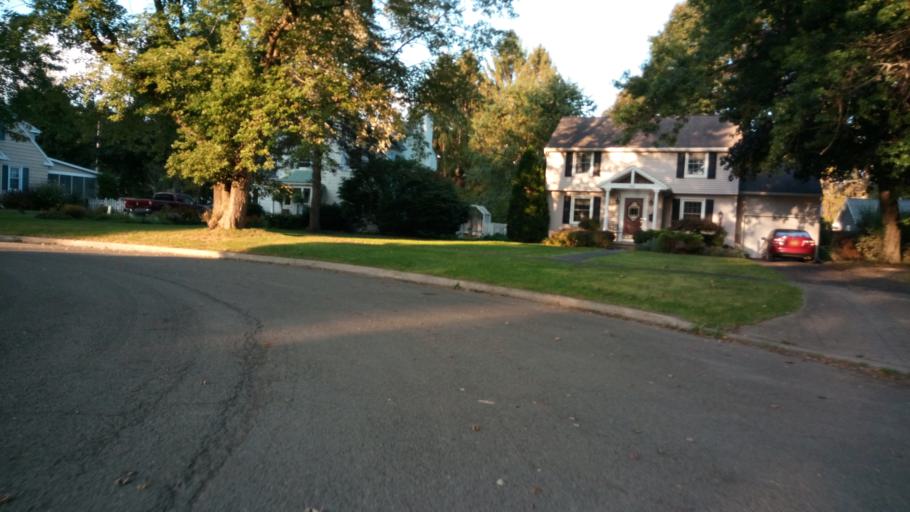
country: US
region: New York
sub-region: Chemung County
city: West Elmira
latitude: 42.0774
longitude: -76.8340
